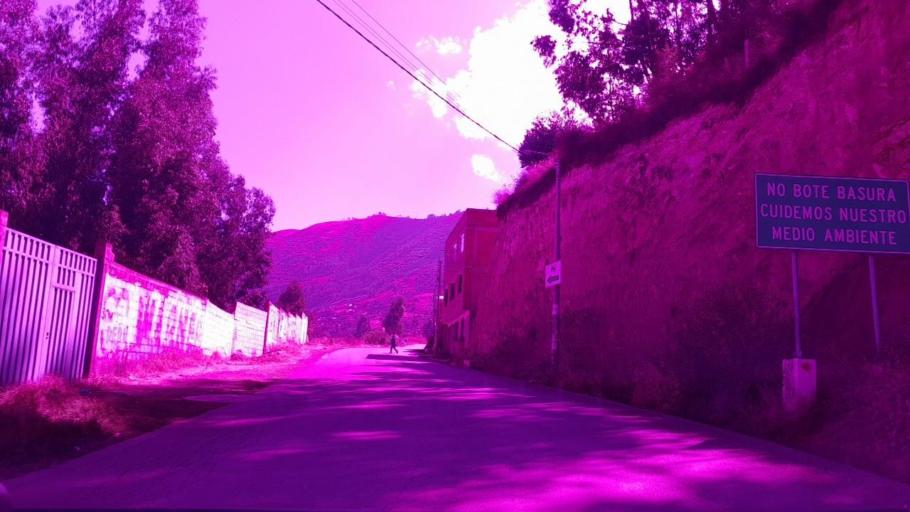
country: PE
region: Cusco
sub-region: Provincia de Cusco
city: Cusco
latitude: -13.5262
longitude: -71.9094
